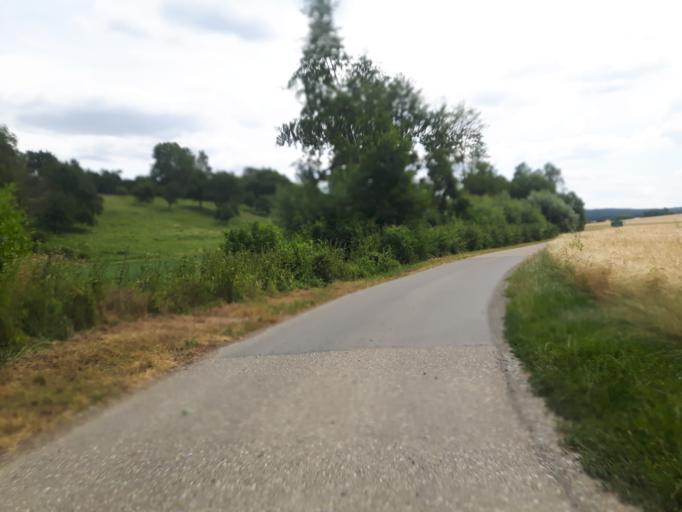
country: DE
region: Baden-Wuerttemberg
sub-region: Regierungsbezirk Stuttgart
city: Eppingen
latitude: 49.1218
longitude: 8.8898
